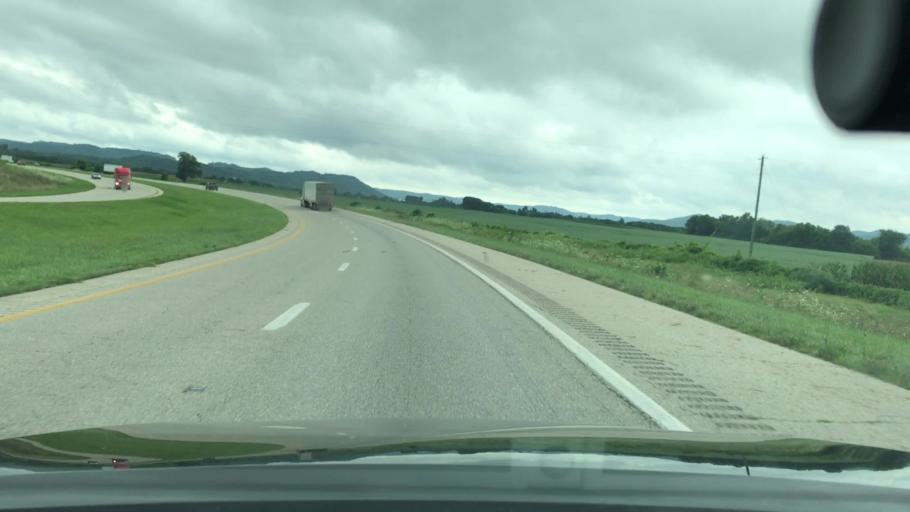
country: US
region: Ohio
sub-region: Ross County
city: Chillicothe
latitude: 39.2721
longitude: -82.8839
